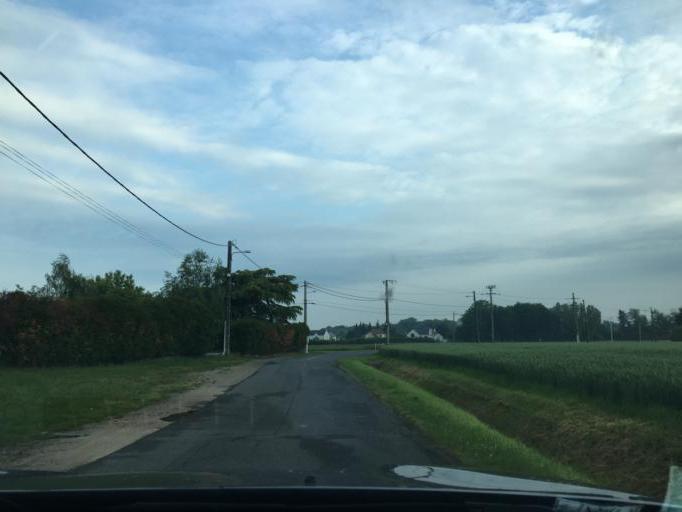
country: FR
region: Centre
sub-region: Departement du Loiret
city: Saint-Denis-en-Val
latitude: 47.8871
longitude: 1.9498
